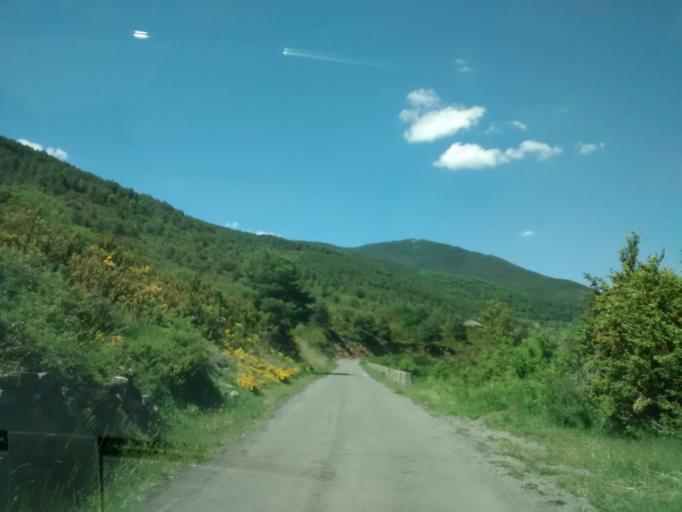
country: ES
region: Aragon
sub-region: Provincia de Huesca
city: Jasa
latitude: 42.6914
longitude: -0.6215
